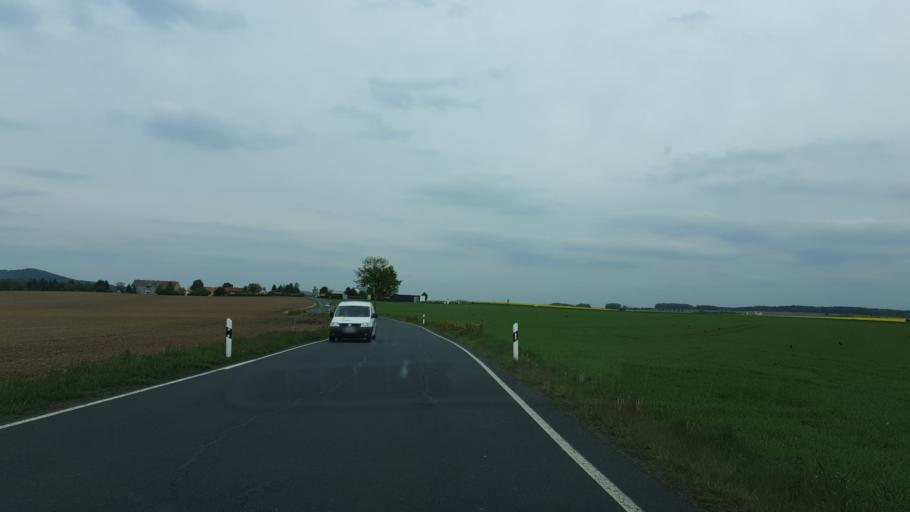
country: DE
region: Saxony
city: Dippoldiswalde
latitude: 50.9083
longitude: 13.6833
